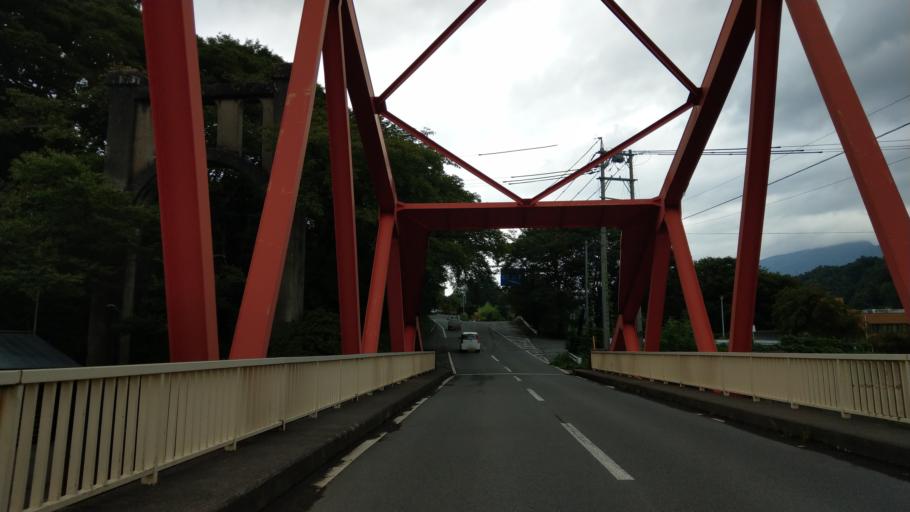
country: JP
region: Nagano
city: Komoro
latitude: 36.3281
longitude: 138.4054
